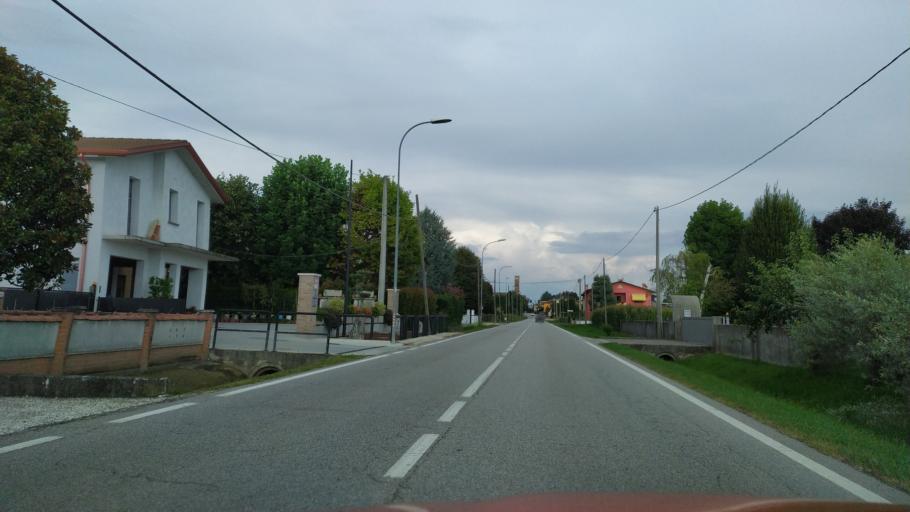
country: IT
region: Veneto
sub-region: Provincia di Padova
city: San Giorgio in Bosco
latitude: 45.5816
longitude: 11.7869
